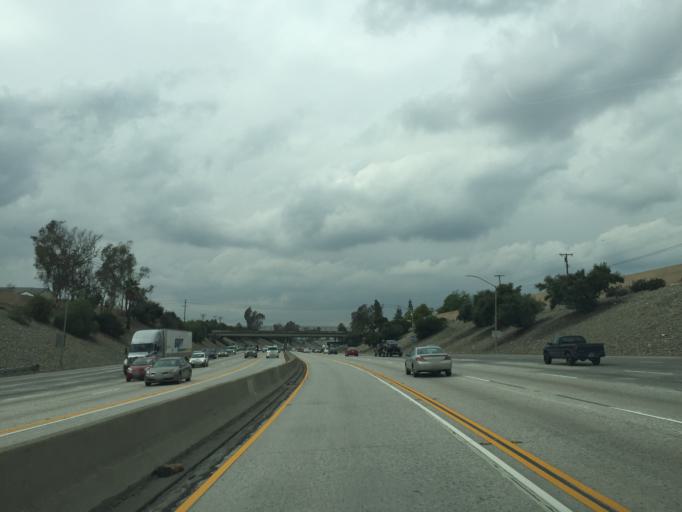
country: US
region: California
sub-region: Los Angeles County
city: Azusa
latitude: 34.1280
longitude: -117.9187
